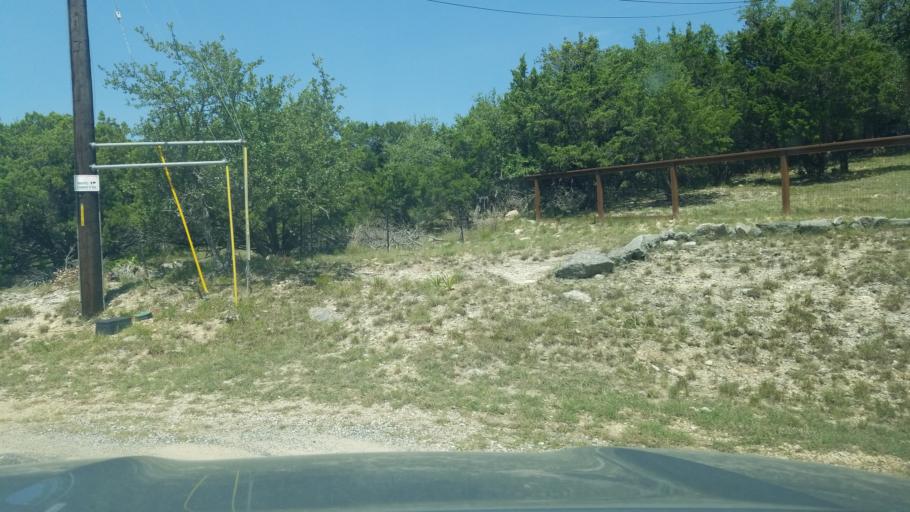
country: US
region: Texas
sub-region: Bexar County
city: Timberwood Park
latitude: 29.6973
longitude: -98.4827
